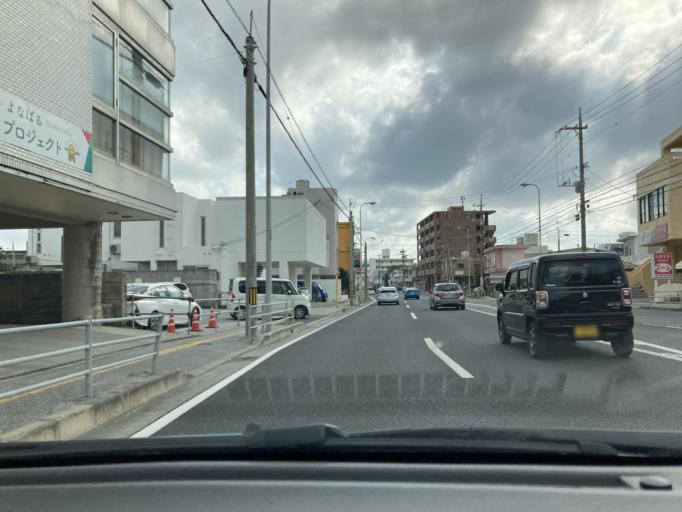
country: JP
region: Okinawa
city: Ginowan
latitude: 26.2077
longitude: 127.7573
